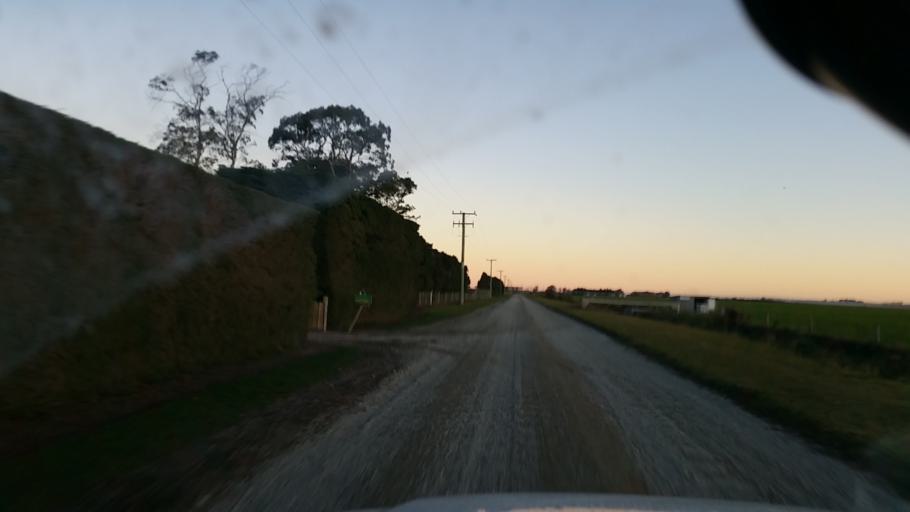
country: NZ
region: Canterbury
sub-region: Ashburton District
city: Tinwald
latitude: -44.0474
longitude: 171.6633
